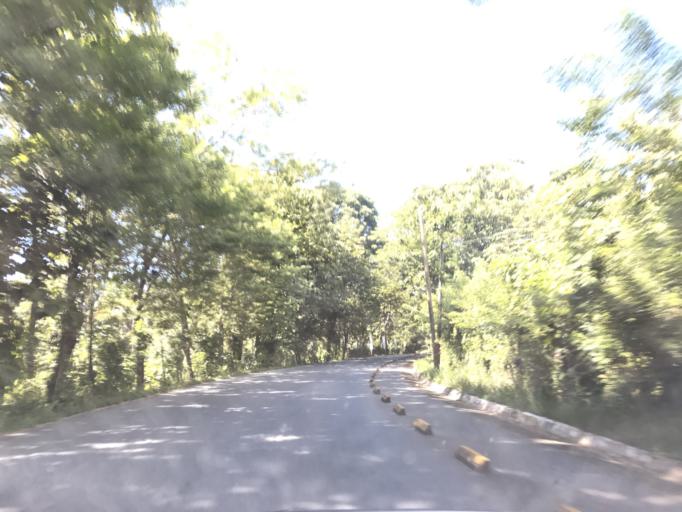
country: GT
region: Izabal
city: Morales
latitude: 15.6535
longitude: -89.0085
